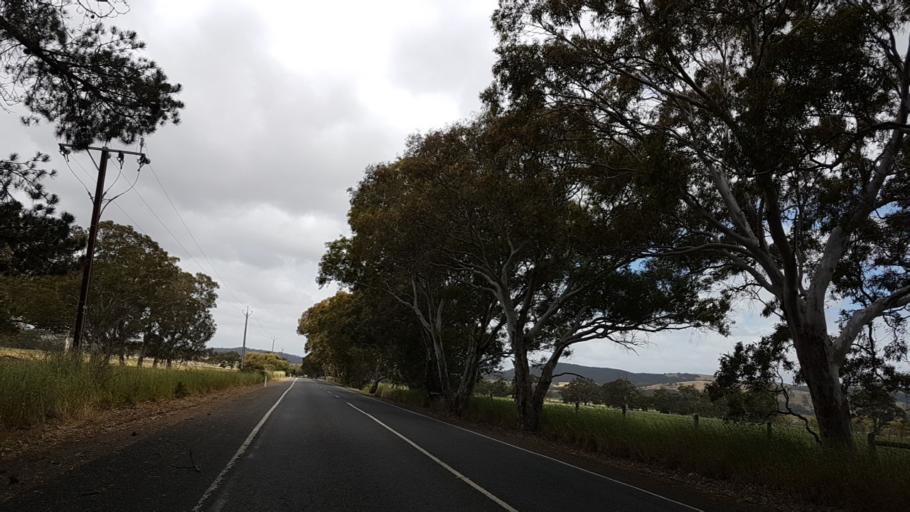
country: AU
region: South Australia
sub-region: Onkaparinga
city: Aldinga
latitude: -35.3786
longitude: 138.4853
